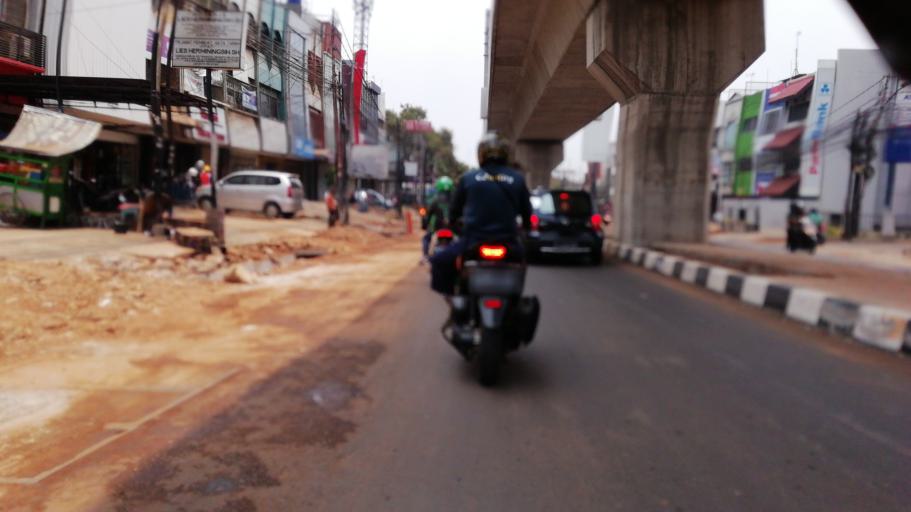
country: ID
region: Banten
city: South Tangerang
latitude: -6.2836
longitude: 106.7959
